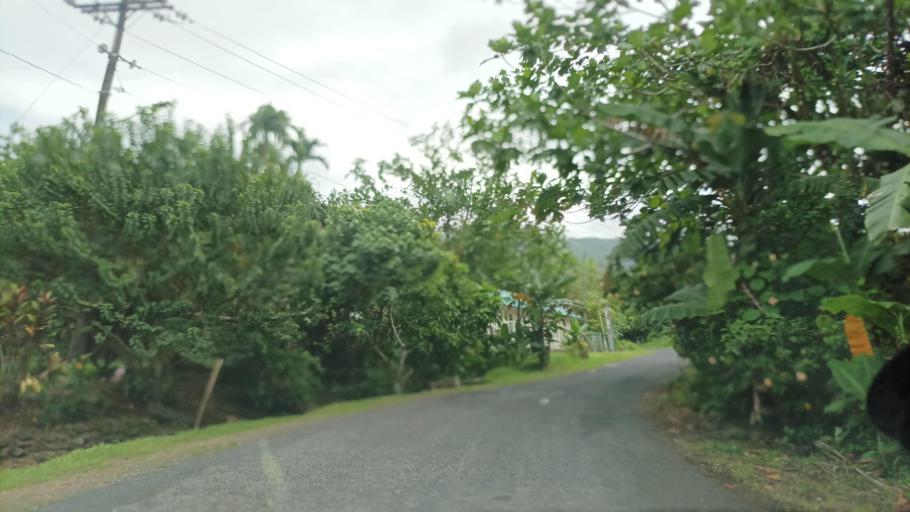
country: FM
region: Pohnpei
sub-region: Madolenihm Municipality
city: Madolenihm Municipality Government
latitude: 6.9140
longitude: 158.2937
